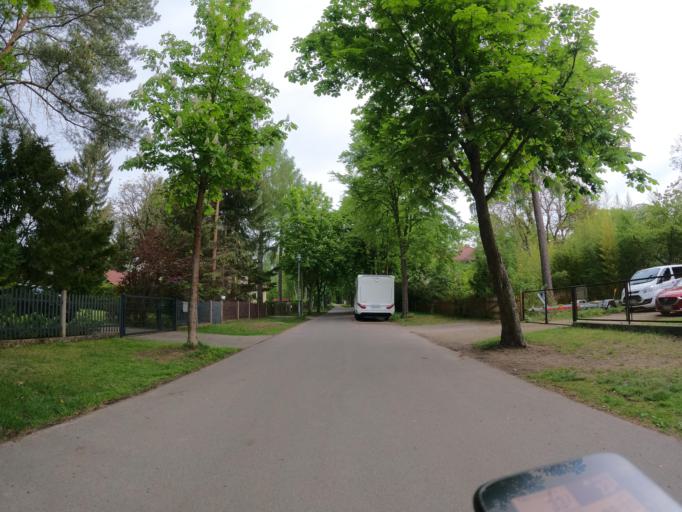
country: DE
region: Brandenburg
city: Konigs Wusterhausen
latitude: 52.2963
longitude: 13.6608
